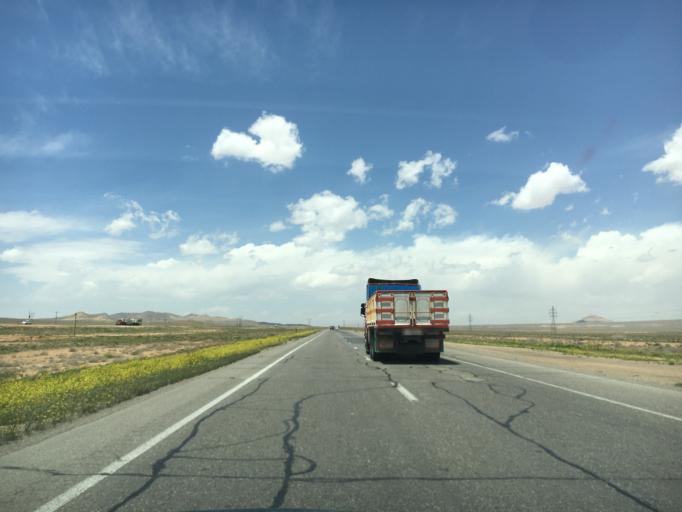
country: IR
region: Isfahan
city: Kashan
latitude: 33.4979
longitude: 51.1190
